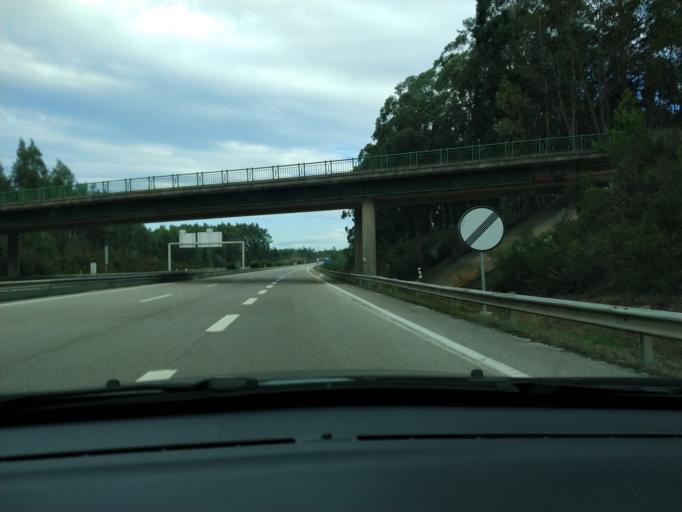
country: PT
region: Aveiro
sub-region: Albergaria-A-Velha
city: Albergaria-a-Velha
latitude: 40.6955
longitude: -8.5228
